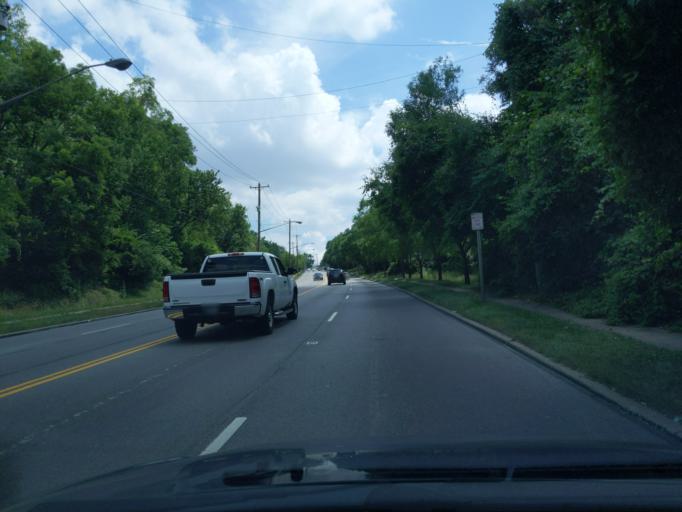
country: US
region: Ohio
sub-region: Hamilton County
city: Saint Bernard
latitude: 39.1385
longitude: -84.5236
